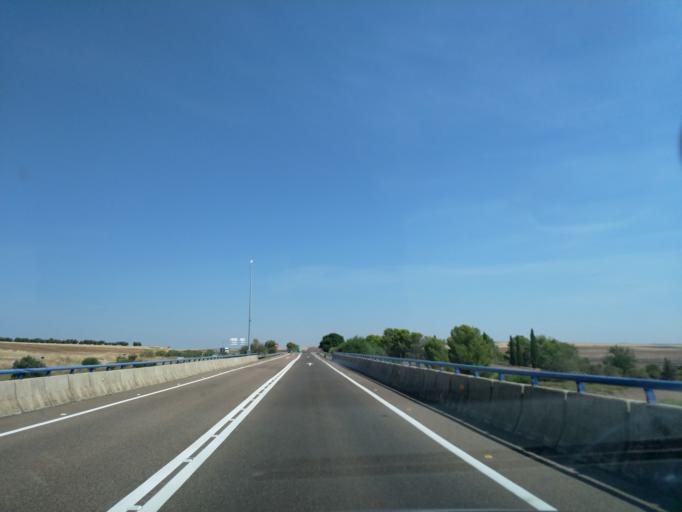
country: ES
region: Extremadura
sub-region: Provincia de Badajoz
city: Merida
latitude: 38.9433
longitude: -6.3424
